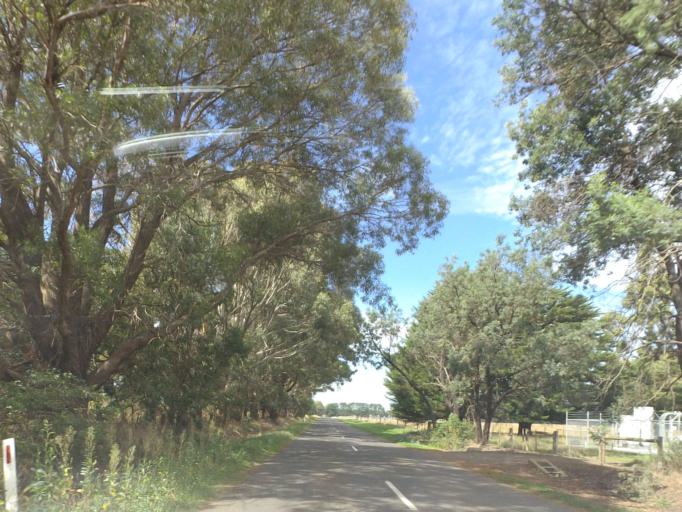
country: AU
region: Victoria
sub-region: Hume
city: Sunbury
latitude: -37.3216
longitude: 144.5274
